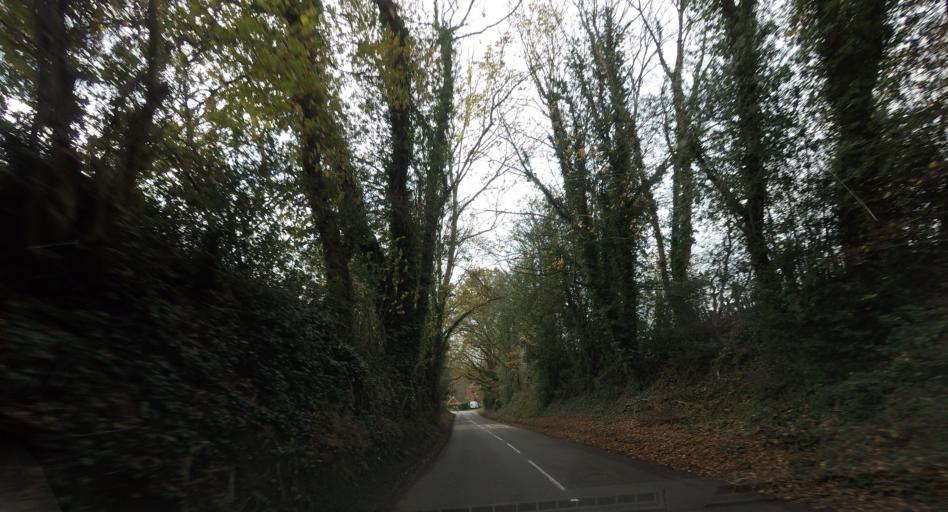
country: GB
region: England
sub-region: Kent
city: Paddock Wood
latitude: 51.1493
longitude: 0.4005
